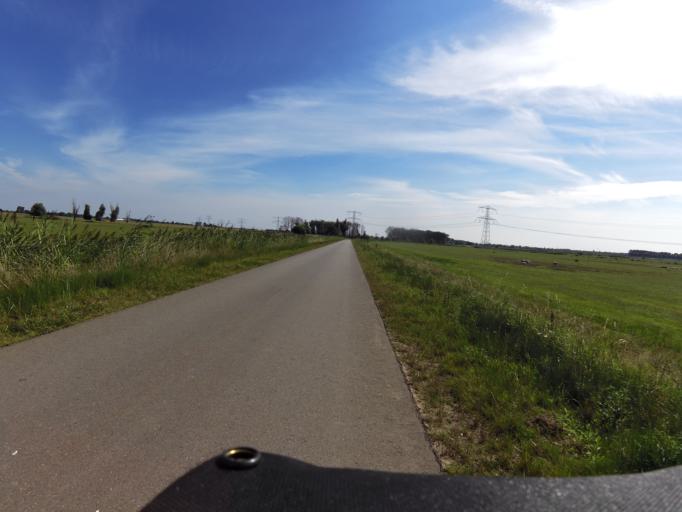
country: NL
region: South Holland
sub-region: Gemeente Hardinxveld-Giessendam
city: Neder-Hardinxveld
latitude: 51.7773
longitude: 4.8379
